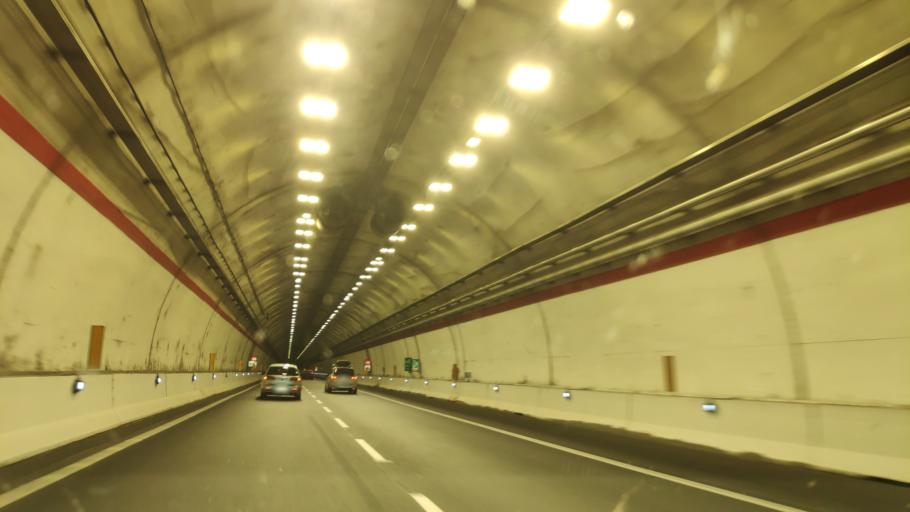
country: IT
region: Campania
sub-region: Provincia di Salerno
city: Petina
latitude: 40.5660
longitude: 15.3741
